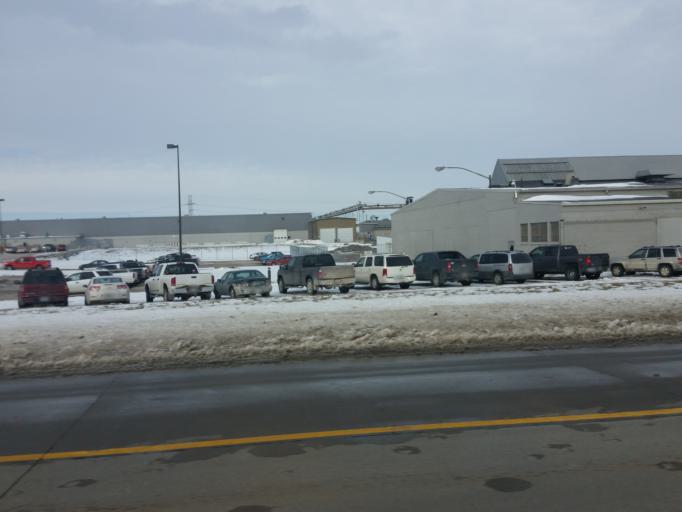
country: US
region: Iowa
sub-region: Black Hawk County
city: Waterloo
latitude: 42.5006
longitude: -92.3501
